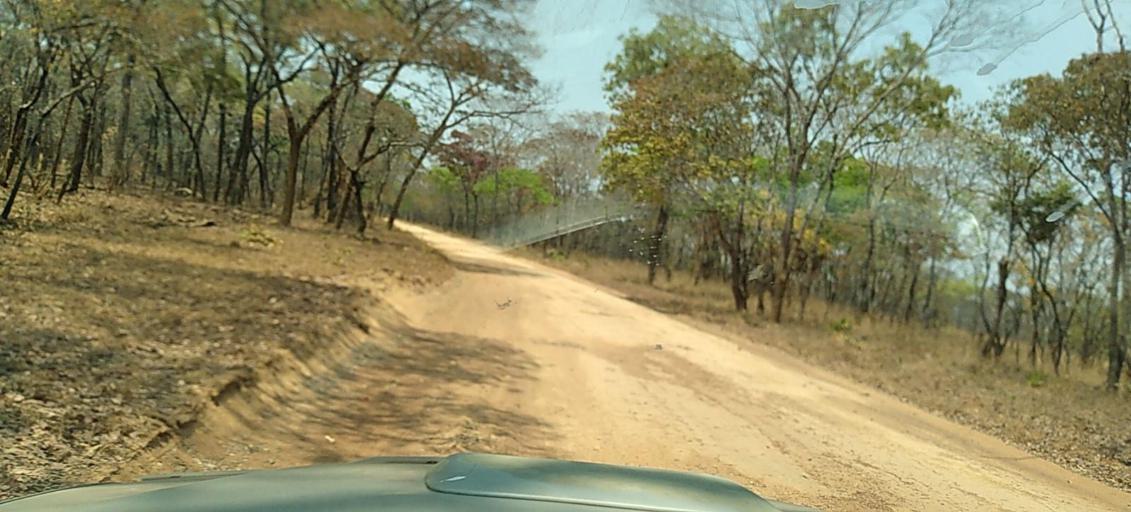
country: ZM
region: North-Western
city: Kasempa
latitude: -13.6088
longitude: 26.1882
